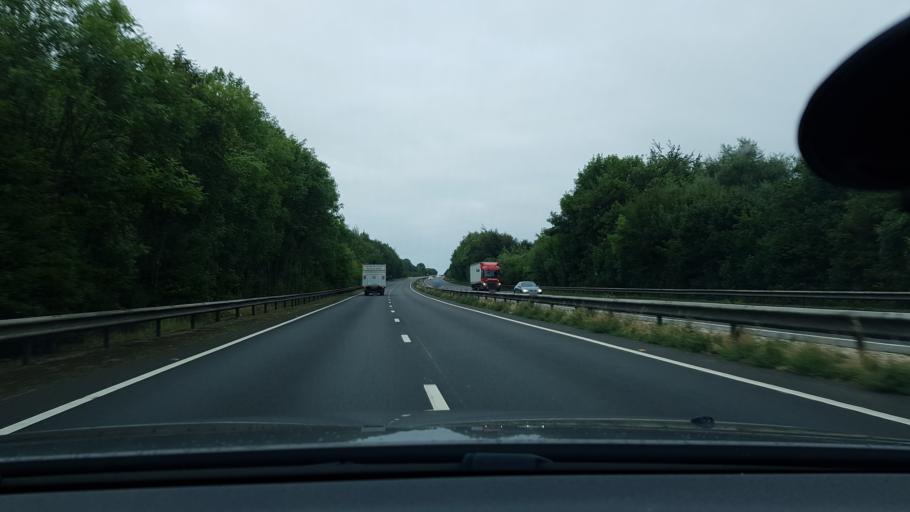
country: GB
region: England
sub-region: Hampshire
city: Overton
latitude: 51.2203
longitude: -1.3429
